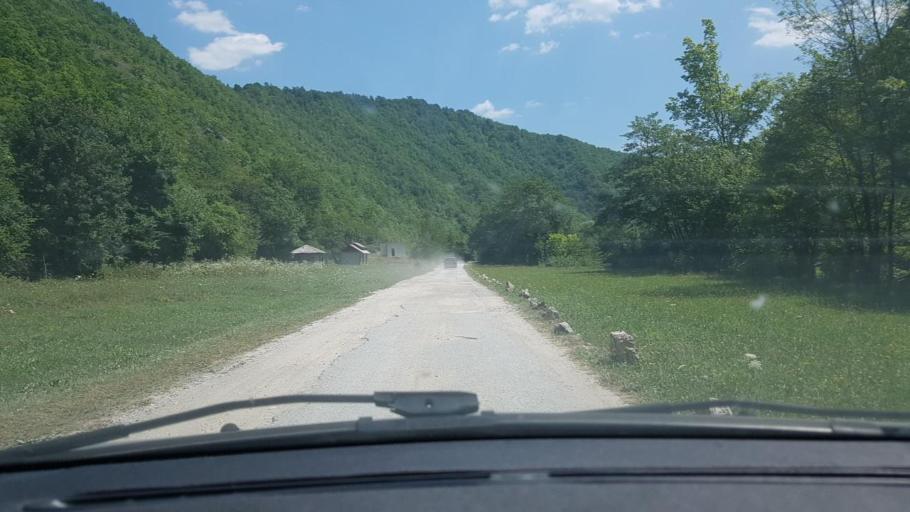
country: BA
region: Federation of Bosnia and Herzegovina
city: Orasac
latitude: 44.6566
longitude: 16.0242
